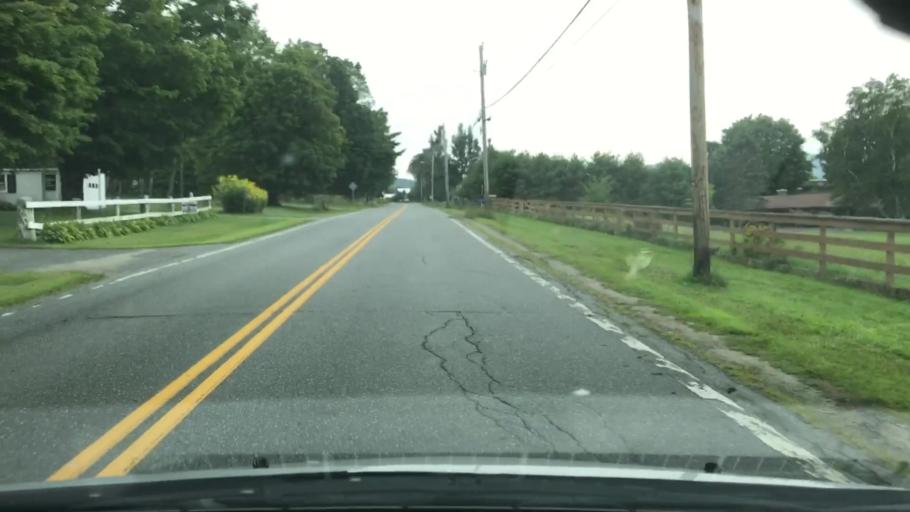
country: US
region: New Hampshire
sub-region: Grafton County
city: Haverhill
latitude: 44.0294
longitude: -72.0669
